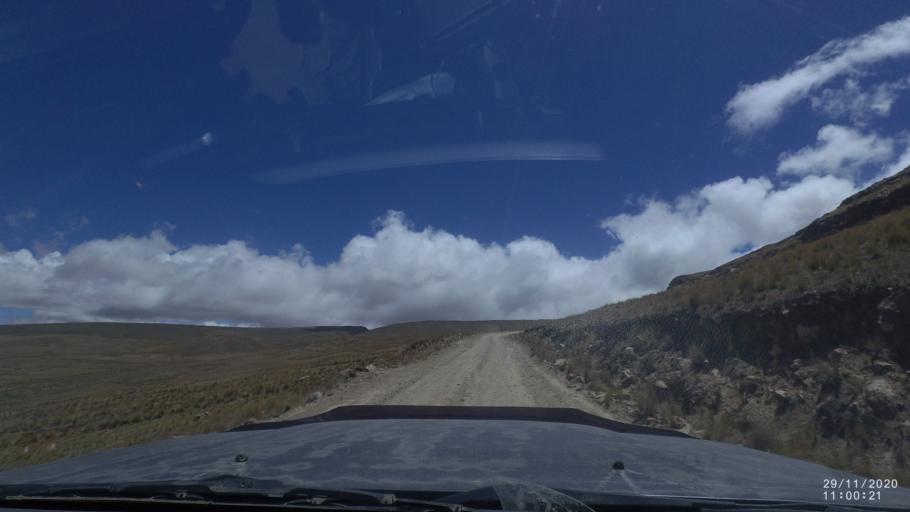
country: BO
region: Cochabamba
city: Cochabamba
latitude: -17.2044
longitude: -66.2266
